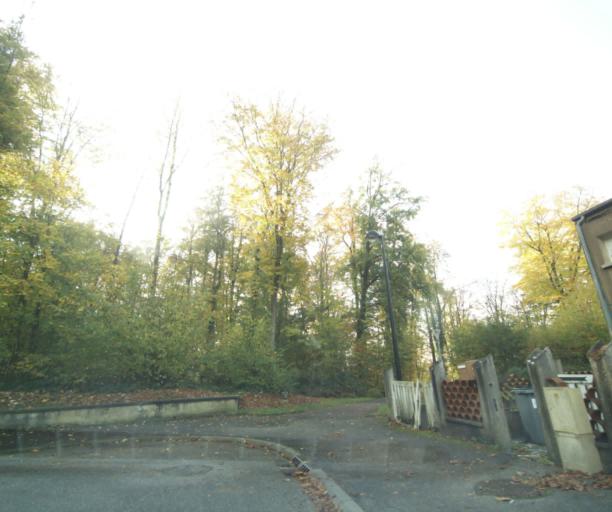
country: FR
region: Lorraine
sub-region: Departement de Meurthe-et-Moselle
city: Briey
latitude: 49.2606
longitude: 5.9261
